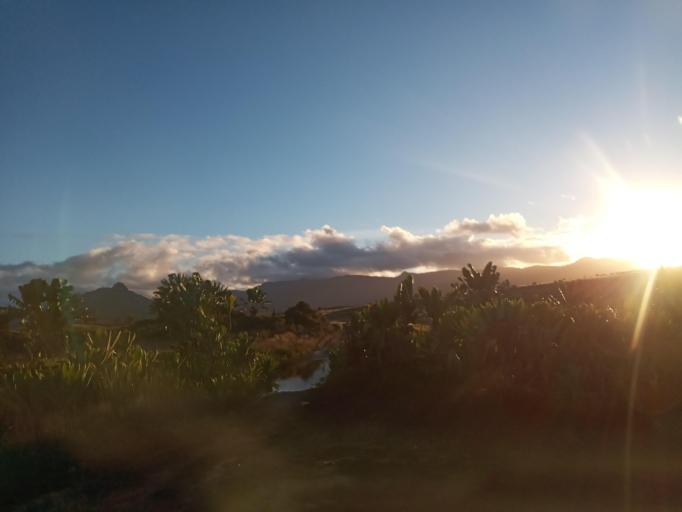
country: MG
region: Anosy
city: Fort Dauphin
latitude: -24.5142
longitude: 47.2494
